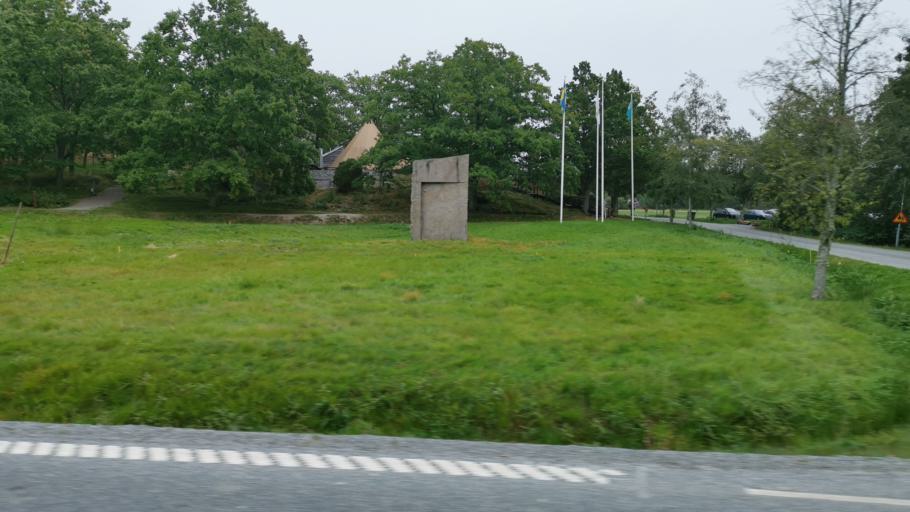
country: SE
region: Vaestra Goetaland
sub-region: Tanums Kommun
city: Tanumshede
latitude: 58.7010
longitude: 11.3387
